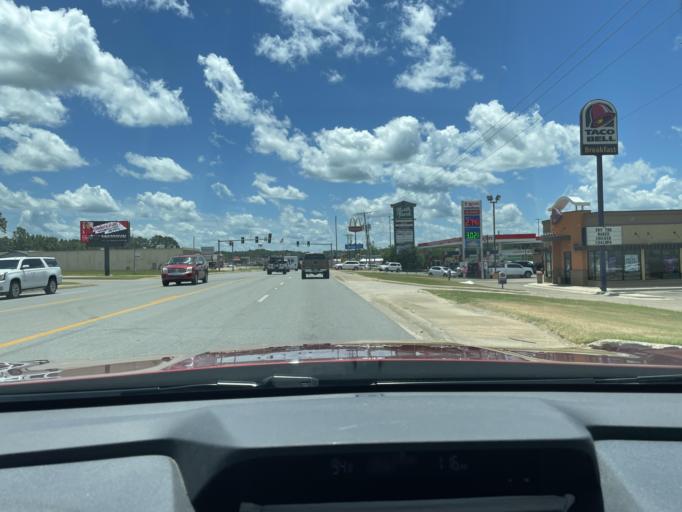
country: US
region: Arkansas
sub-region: Drew County
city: Monticello
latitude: 33.6374
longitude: -91.8016
